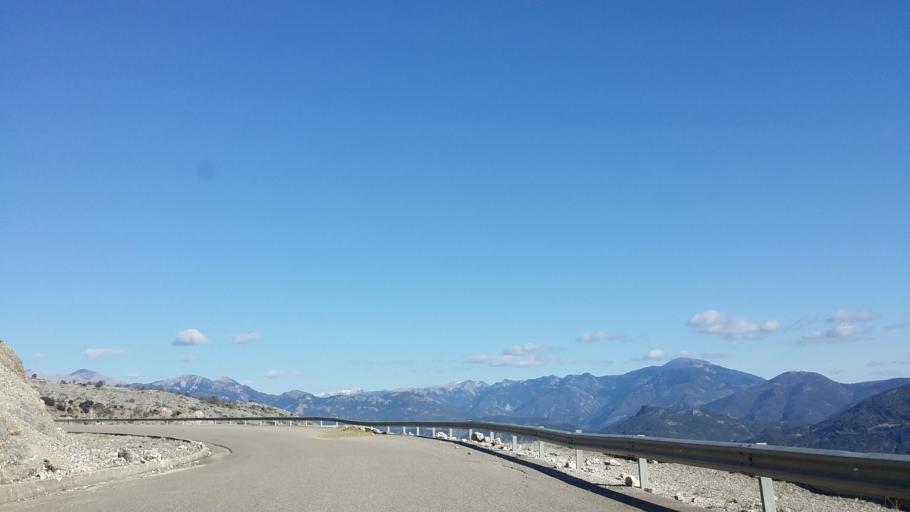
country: GR
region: Central Greece
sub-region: Nomos Evrytanias
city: Kerasochori
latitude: 38.9539
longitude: 21.4671
